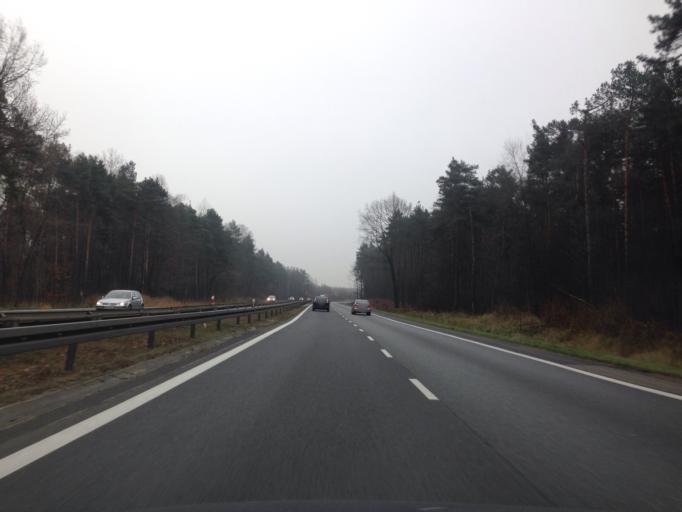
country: PL
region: Silesian Voivodeship
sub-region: Powiat myszkowski
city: Kozieglowy
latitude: 50.5391
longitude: 19.1831
